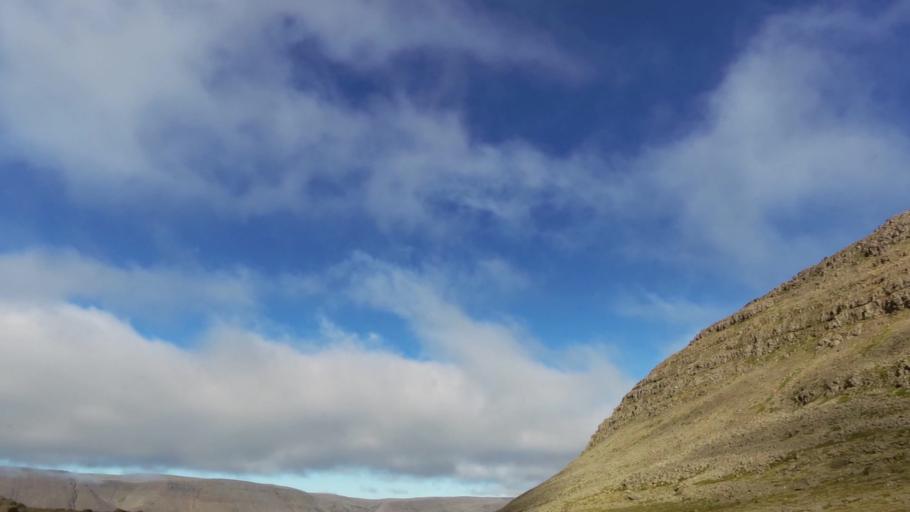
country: IS
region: West
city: Olafsvik
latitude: 65.5756
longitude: -24.0814
